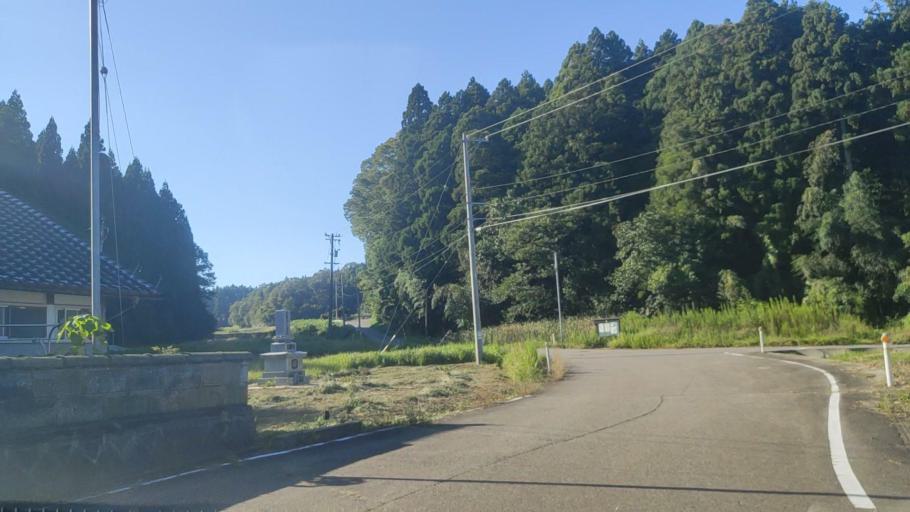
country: JP
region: Ishikawa
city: Nanao
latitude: 37.1282
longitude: 136.8956
